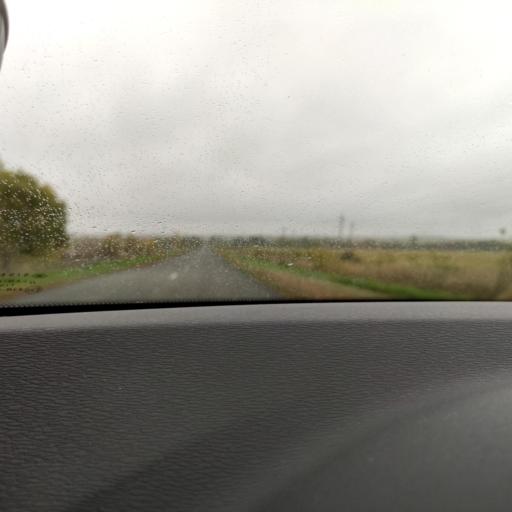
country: RU
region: Samara
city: Yelkhovka
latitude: 53.7388
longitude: 50.2899
